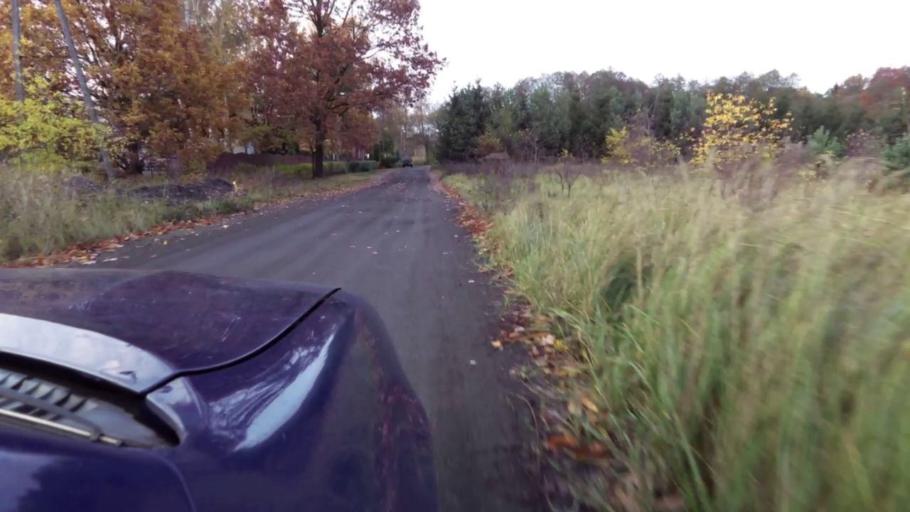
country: PL
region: West Pomeranian Voivodeship
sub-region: Powiat goleniowski
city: Goleniow
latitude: 53.6078
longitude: 14.7535
